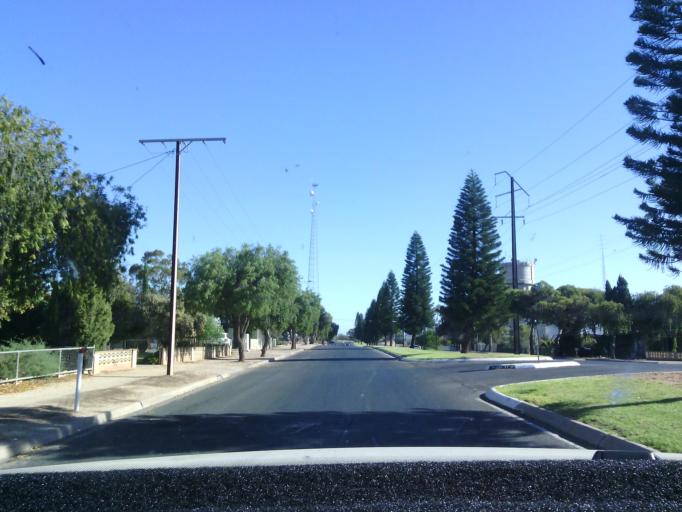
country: AU
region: South Australia
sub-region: Berri and Barmera
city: Berri
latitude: -34.2751
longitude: 140.5971
